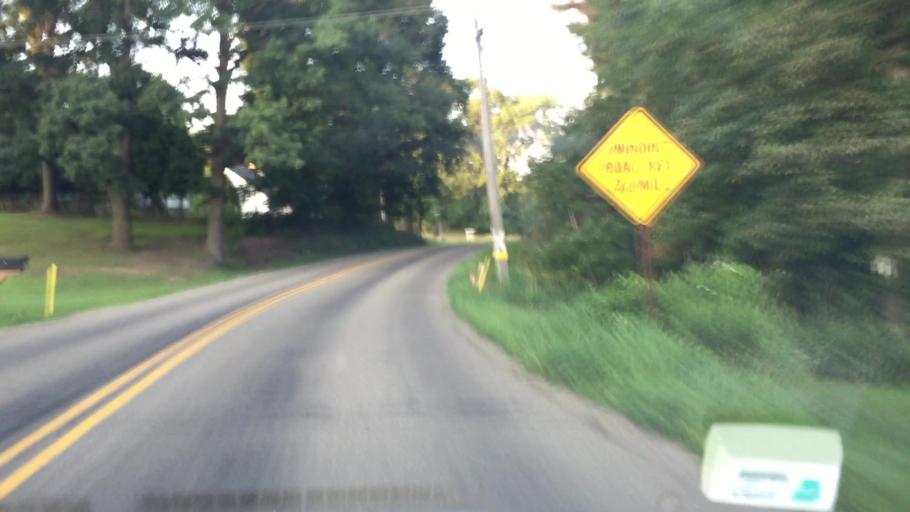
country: US
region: Pennsylvania
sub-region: Butler County
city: Seven Fields
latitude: 40.7197
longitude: -80.0424
